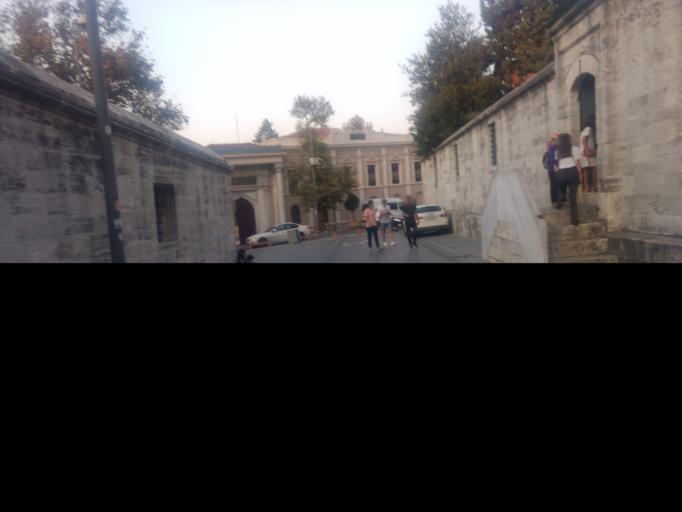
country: TR
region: Istanbul
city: Eminoenue
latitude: 41.0171
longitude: 28.9632
